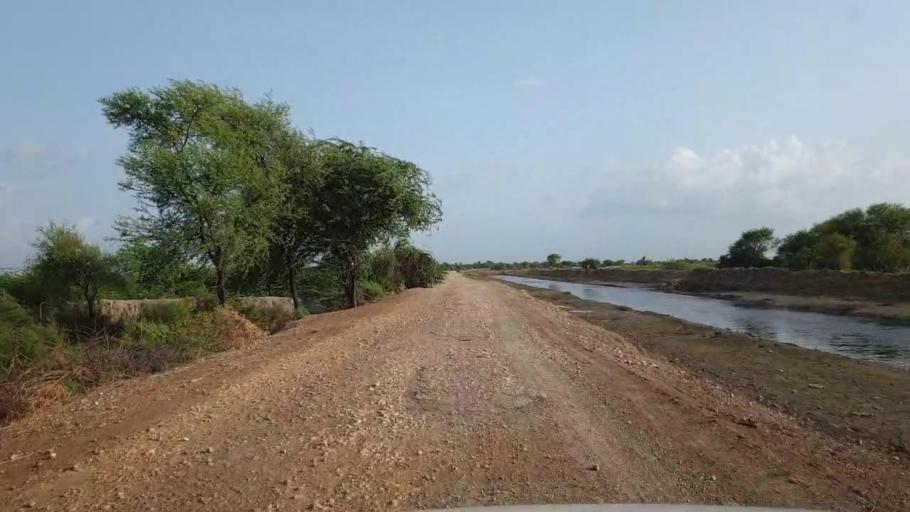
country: PK
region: Sindh
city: Kario
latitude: 24.8472
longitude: 68.6522
